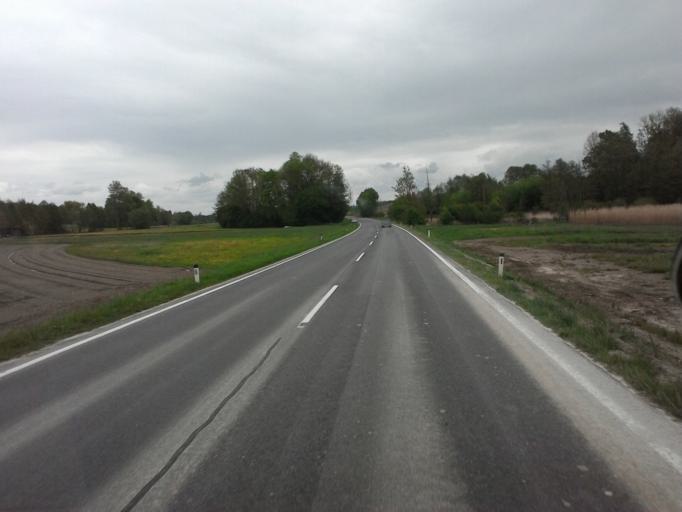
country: AT
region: Upper Austria
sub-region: Politischer Bezirk Vocklabruck
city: Wolfsegg am Hausruck
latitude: 48.2193
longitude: 13.7041
